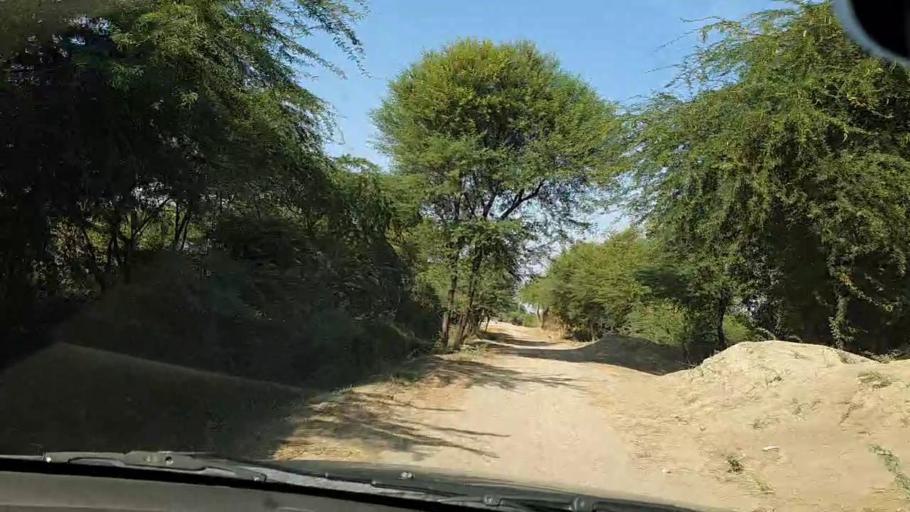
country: PK
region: Sindh
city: Mirpur Batoro
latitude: 24.6508
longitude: 68.2545
